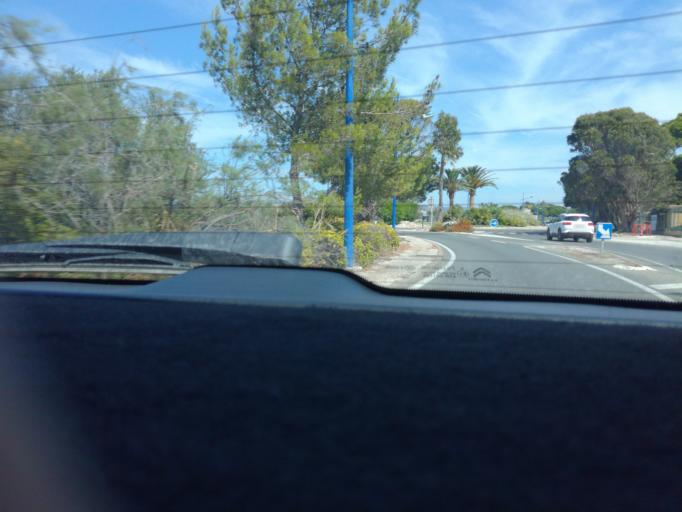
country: FR
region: Provence-Alpes-Cote d'Azur
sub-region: Departement du Var
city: Hyeres
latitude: 43.0799
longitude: 6.1495
